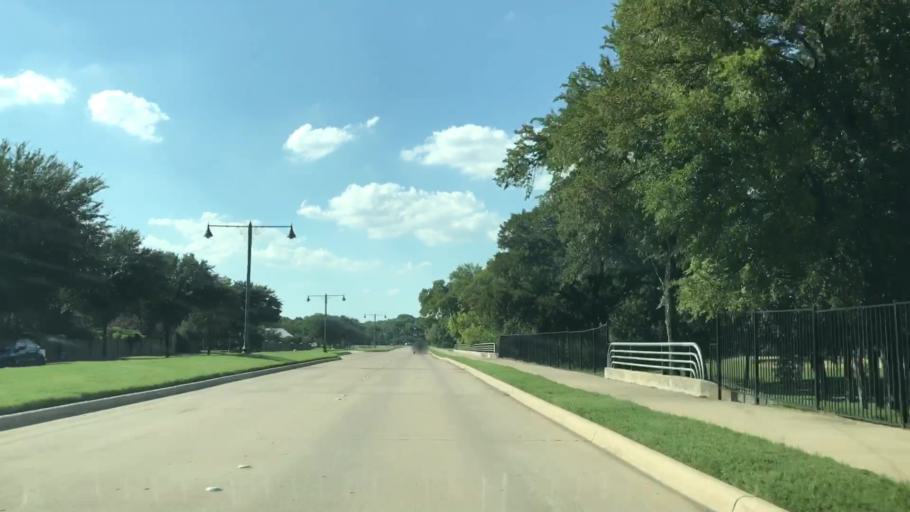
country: US
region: Texas
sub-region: Tarrant County
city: Keller
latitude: 32.9247
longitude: -97.2167
